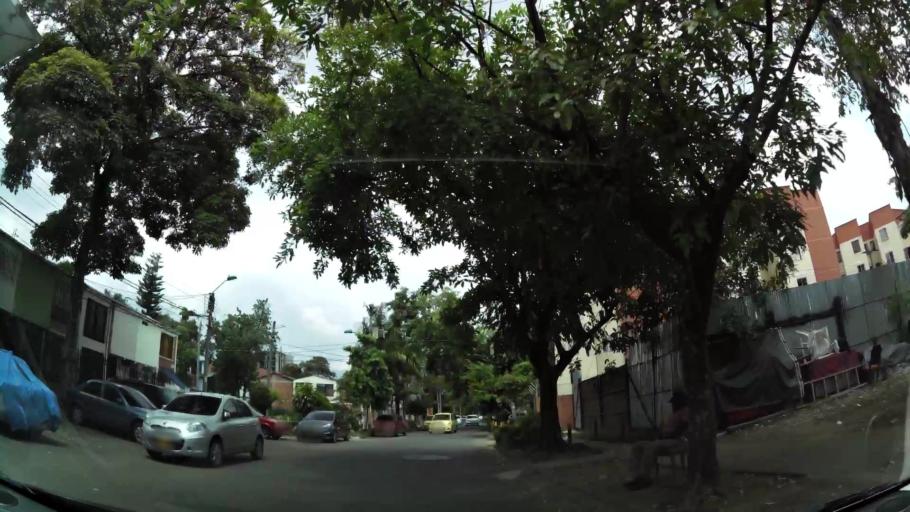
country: CO
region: Valle del Cauca
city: Cali
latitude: 3.4778
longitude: -76.4983
